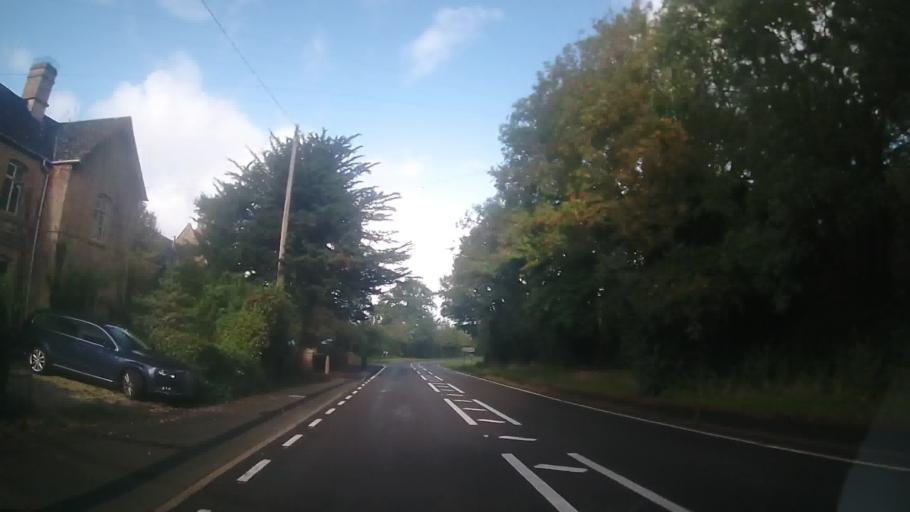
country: GB
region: England
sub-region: Gloucestershire
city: Moreton in Marsh
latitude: 51.9676
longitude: -1.6250
